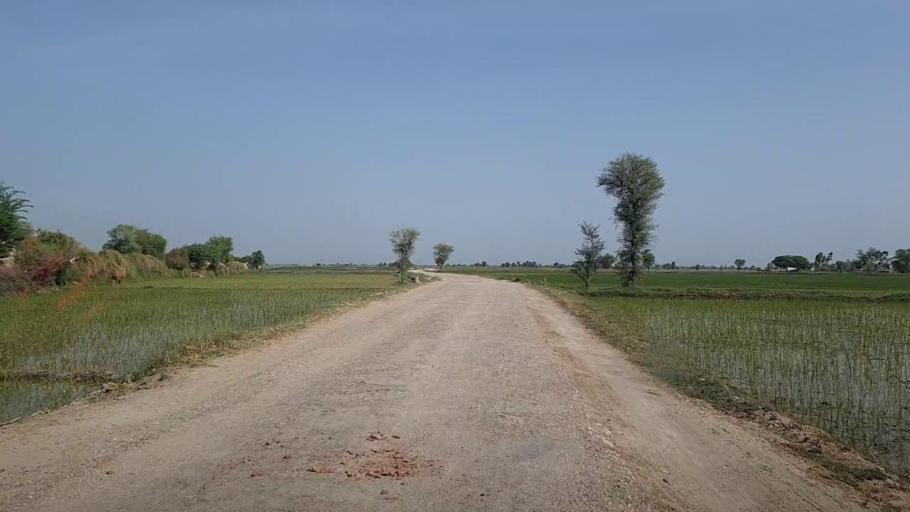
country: PK
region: Sindh
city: Mehar
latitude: 27.1153
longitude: 67.8435
